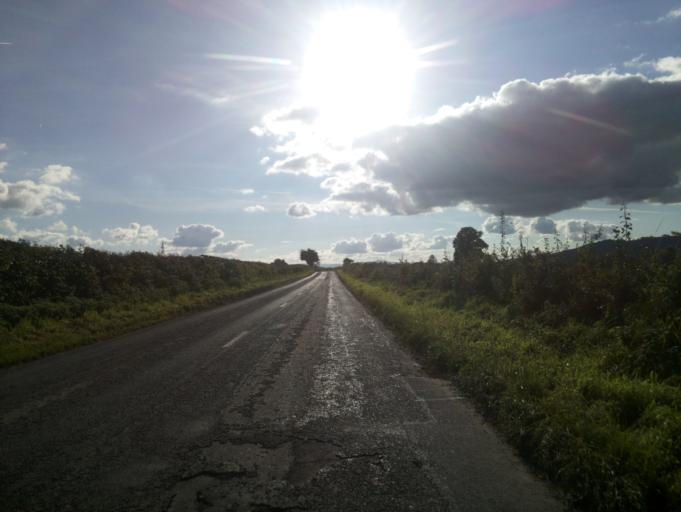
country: GB
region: England
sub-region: Herefordshire
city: Clifford
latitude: 52.0955
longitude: -3.1098
